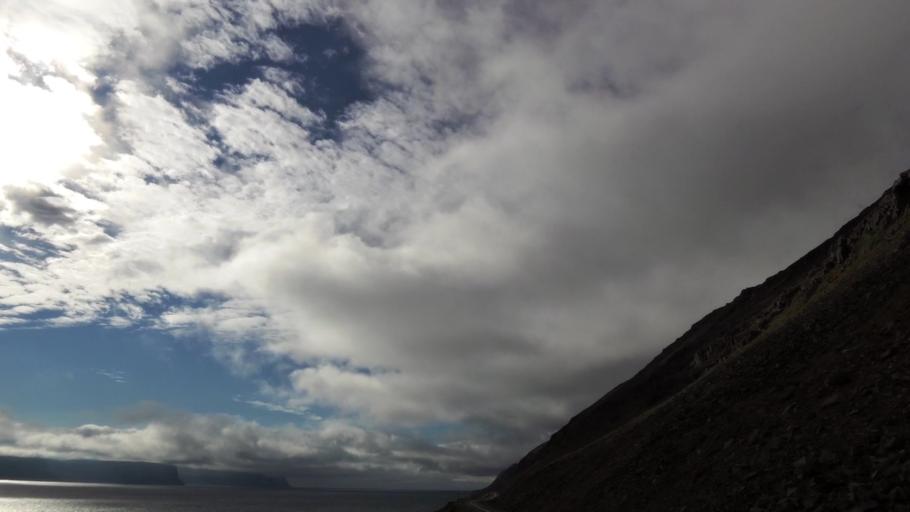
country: IS
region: West
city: Olafsvik
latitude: 65.5597
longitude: -23.9070
